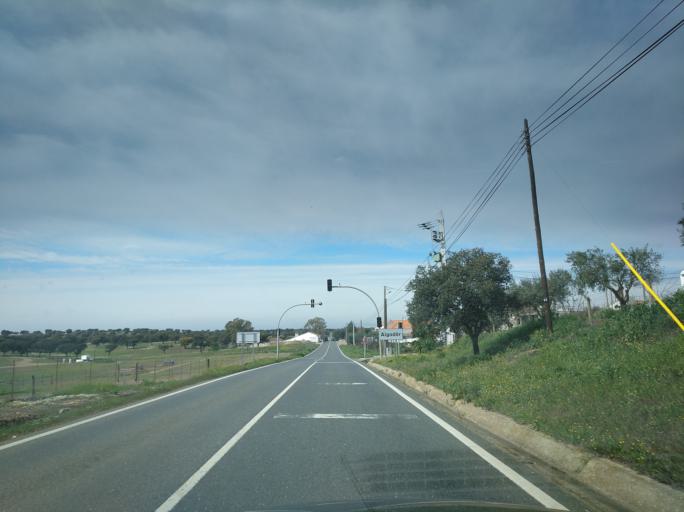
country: PT
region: Beja
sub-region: Mertola
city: Mertola
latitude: 37.7426
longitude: -7.7917
